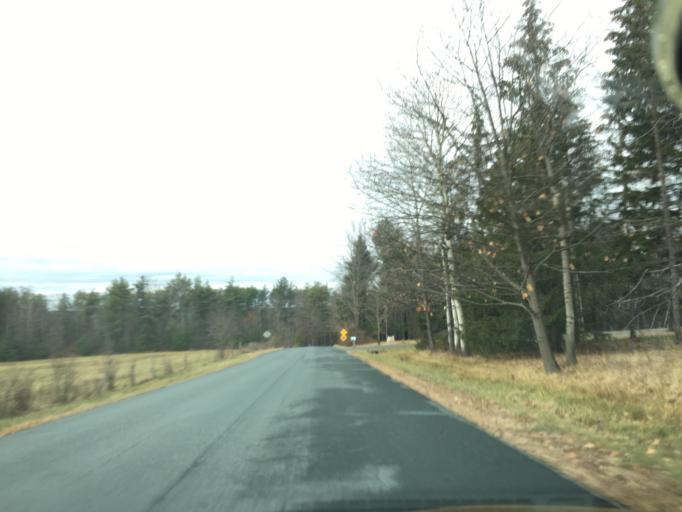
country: US
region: New York
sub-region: Rensselaer County
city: Averill Park
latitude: 42.6112
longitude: -73.5475
